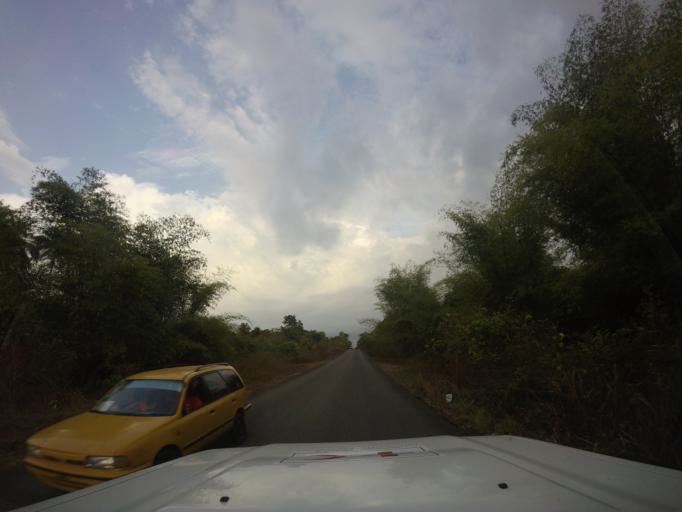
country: LR
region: Bomi
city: Tubmanburg
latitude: 6.6951
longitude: -10.9007
